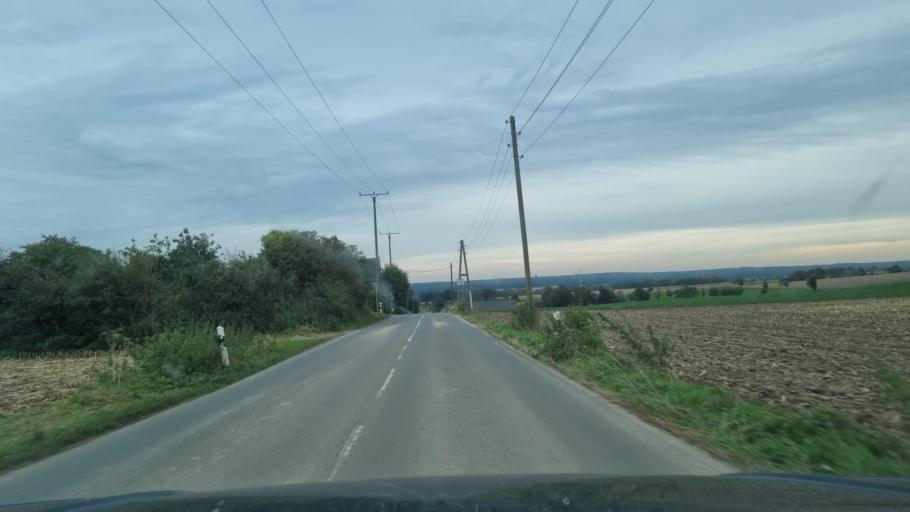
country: DE
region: North Rhine-Westphalia
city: Kalkar
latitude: 51.7059
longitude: 6.3062
